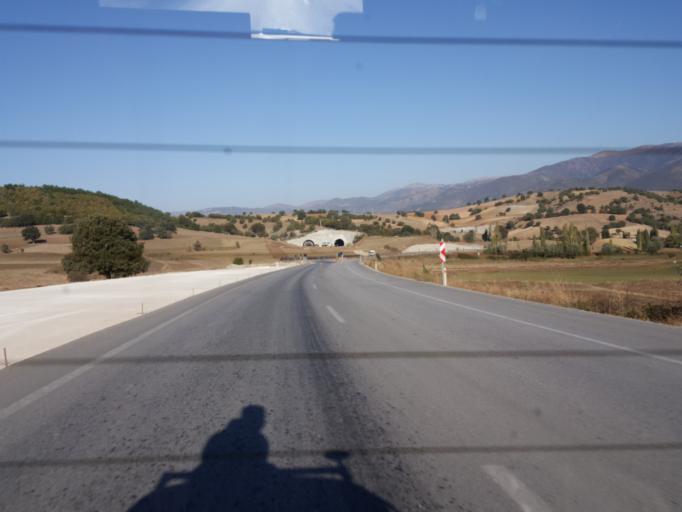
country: TR
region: Amasya
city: Ezinepazari
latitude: 40.5522
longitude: 36.1427
